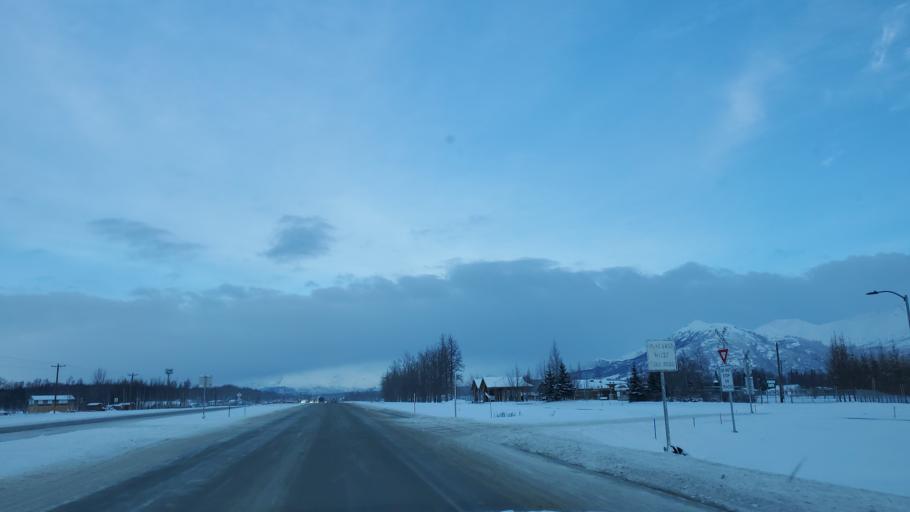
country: US
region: Alaska
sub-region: Matanuska-Susitna Borough
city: Palmer
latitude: 61.5775
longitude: -149.1407
